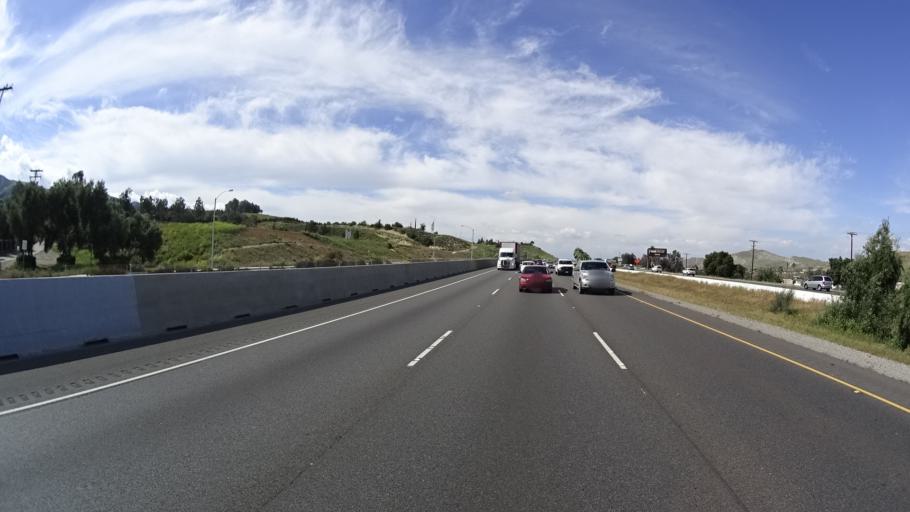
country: US
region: California
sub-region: Riverside County
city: El Cerrito
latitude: 33.8005
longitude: -117.5040
